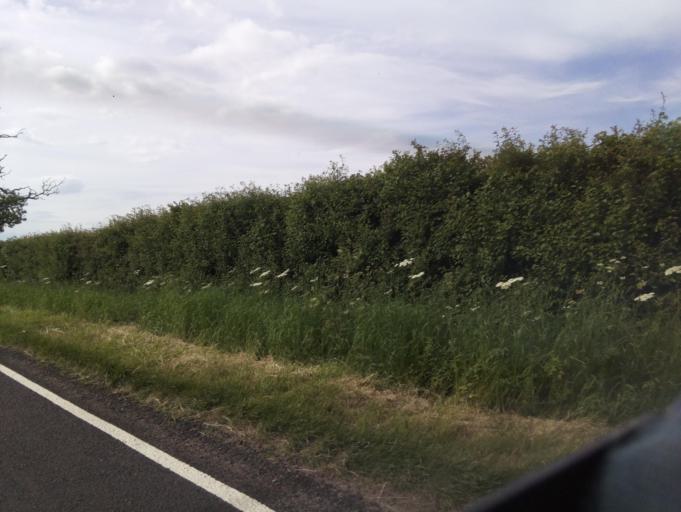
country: GB
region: England
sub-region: Worcestershire
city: Broadway
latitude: 52.0805
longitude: -1.8484
